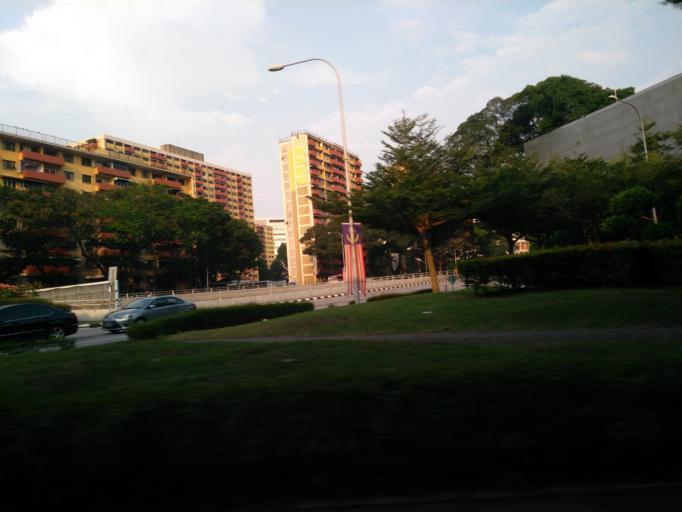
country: MY
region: Kuala Lumpur
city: Kuala Lumpur
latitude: 3.1361
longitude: 101.7039
